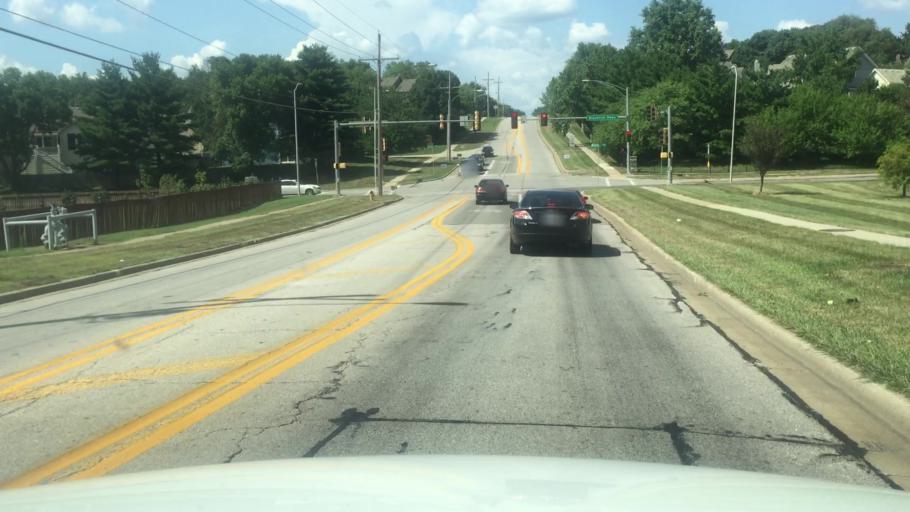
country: US
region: Kansas
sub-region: Johnson County
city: Lenexa
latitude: 38.9947
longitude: -94.7423
